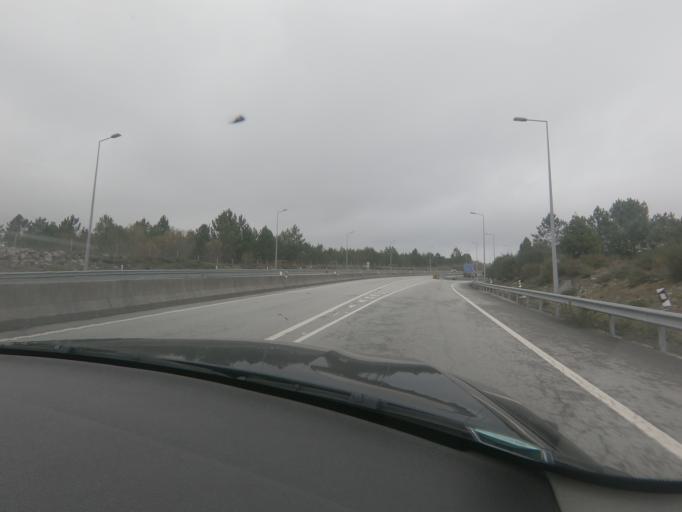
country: PT
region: Viseu
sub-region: Viseu
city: Abraveses
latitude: 40.6752
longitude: -7.9705
